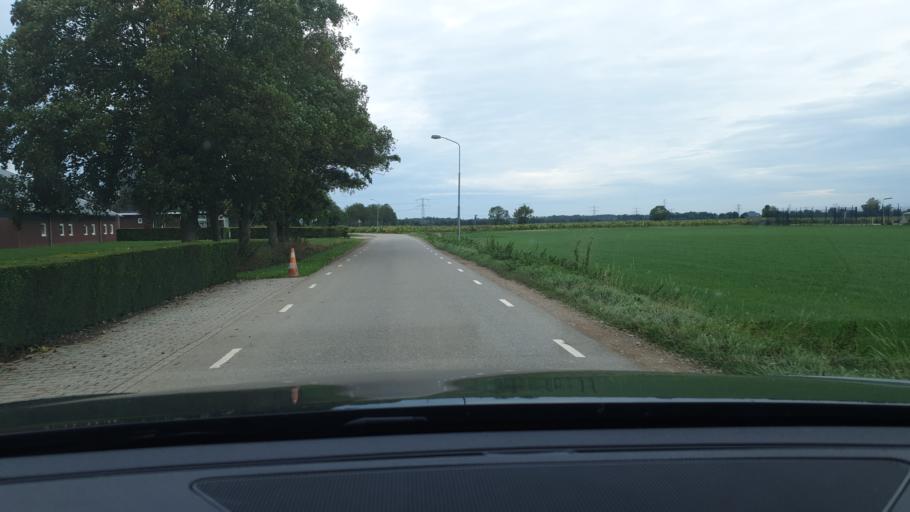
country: NL
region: Gelderland
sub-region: Gemeente Overbetuwe
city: Oosterhout
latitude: 51.8979
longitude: 5.8206
